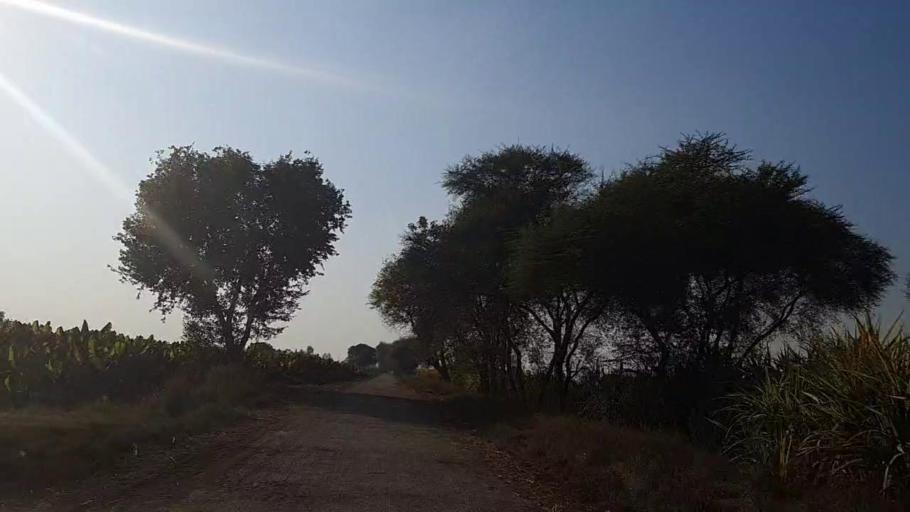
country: PK
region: Sindh
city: Daur
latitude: 26.3329
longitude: 68.1497
